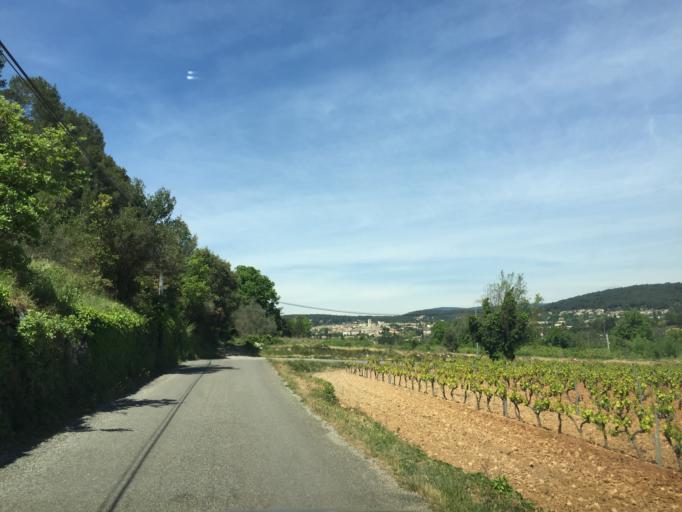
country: FR
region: Provence-Alpes-Cote d'Azur
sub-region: Departement du Var
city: Lorgues
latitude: 43.4786
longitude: 6.3676
